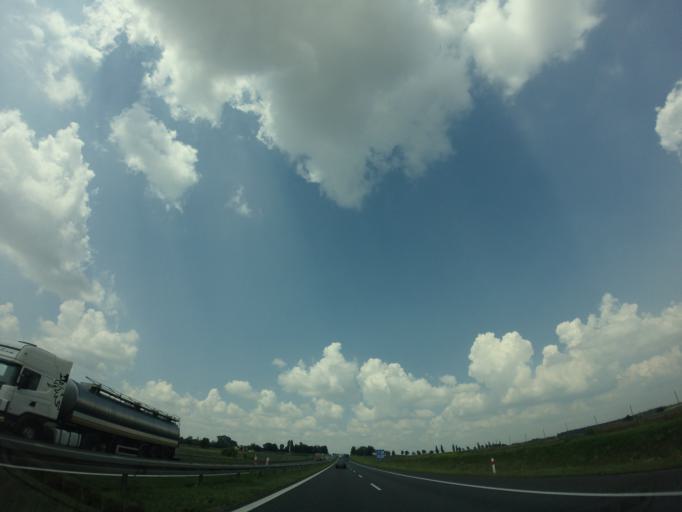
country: PL
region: Silesian Voivodeship
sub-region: Powiat gliwicki
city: Rudziniec
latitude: 50.4076
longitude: 18.4156
